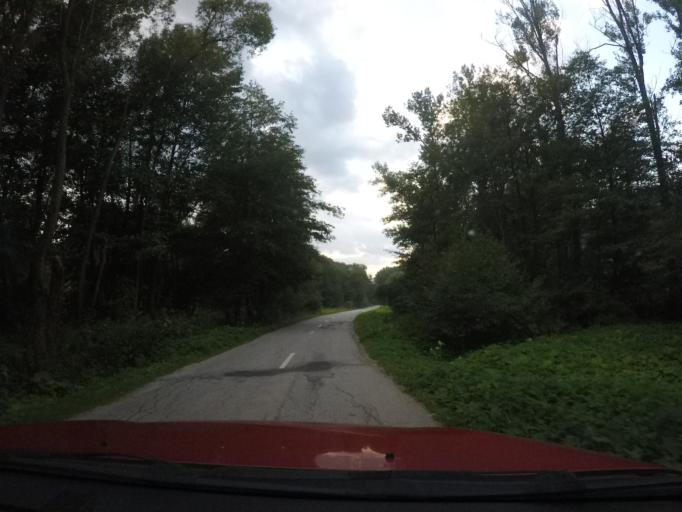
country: SK
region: Kosicky
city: Medzev
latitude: 48.6288
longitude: 20.7394
